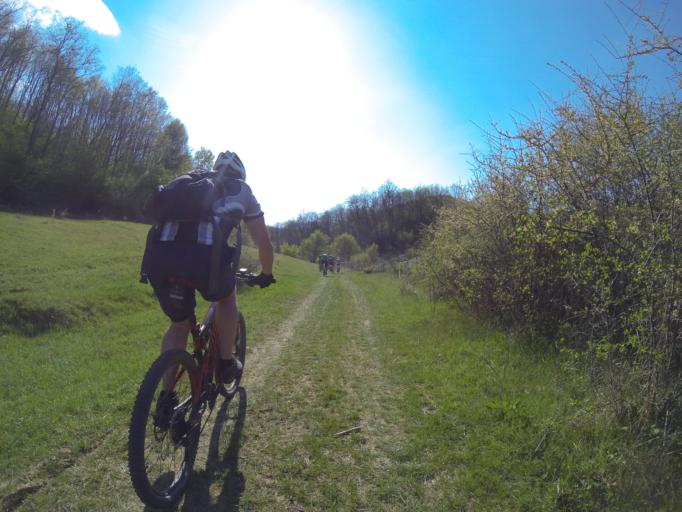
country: RO
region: Gorj
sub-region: Comuna Crusetu
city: Crusetu
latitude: 44.6238
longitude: 23.6273
